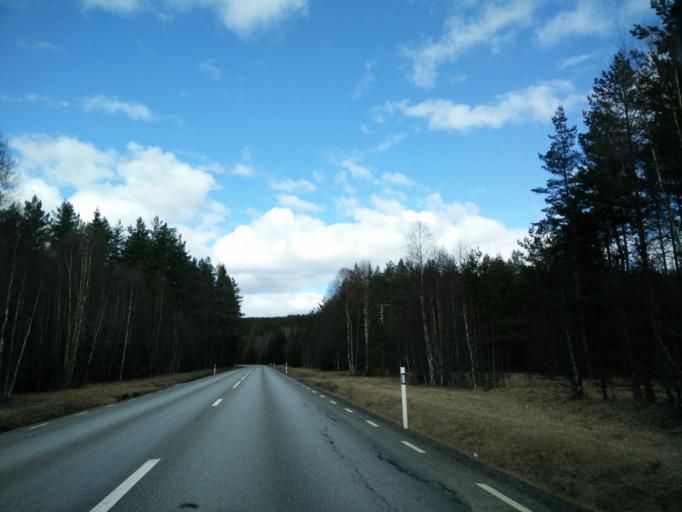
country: SE
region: Vaermland
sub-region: Munkfors Kommun
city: Munkfors
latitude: 59.9427
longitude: 13.5812
